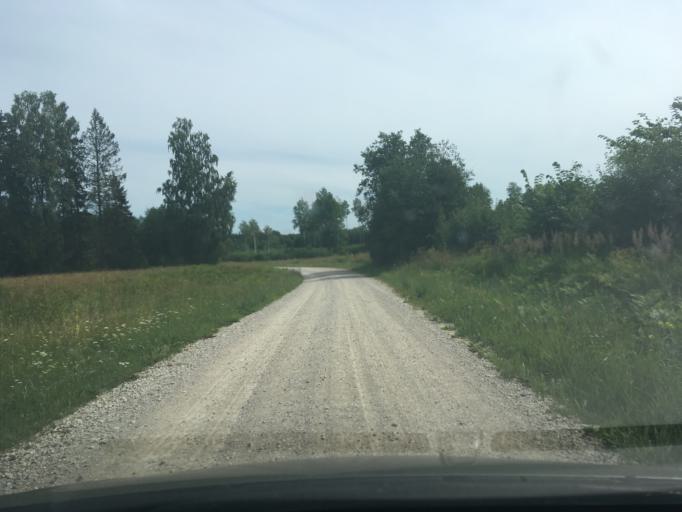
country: EE
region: Raplamaa
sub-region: Maerjamaa vald
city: Marjamaa
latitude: 58.9528
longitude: 24.5796
